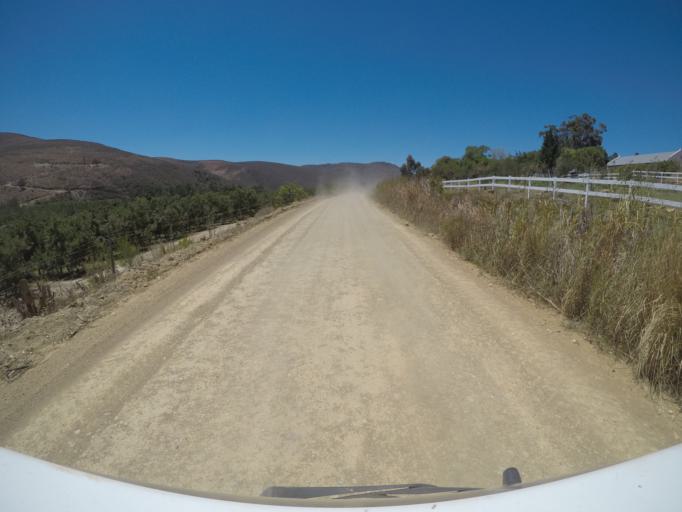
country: ZA
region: Western Cape
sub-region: Overberg District Municipality
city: Grabouw
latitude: -34.1141
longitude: 19.2216
